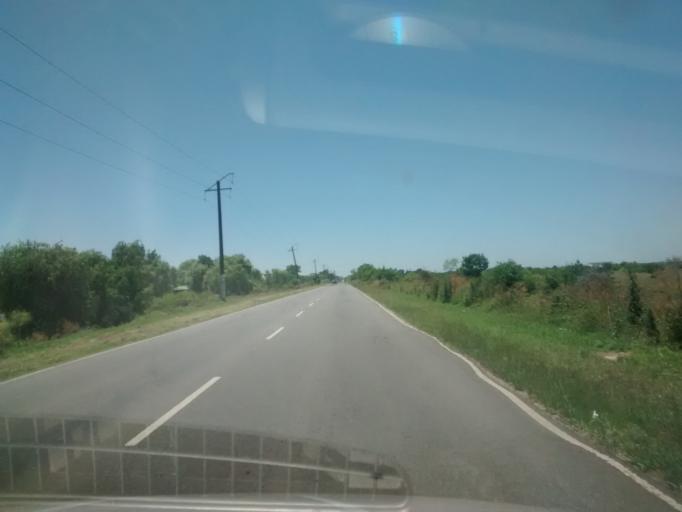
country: AR
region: Buenos Aires
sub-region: Partido de Berisso
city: Berisso
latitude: -34.8887
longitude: -57.8660
